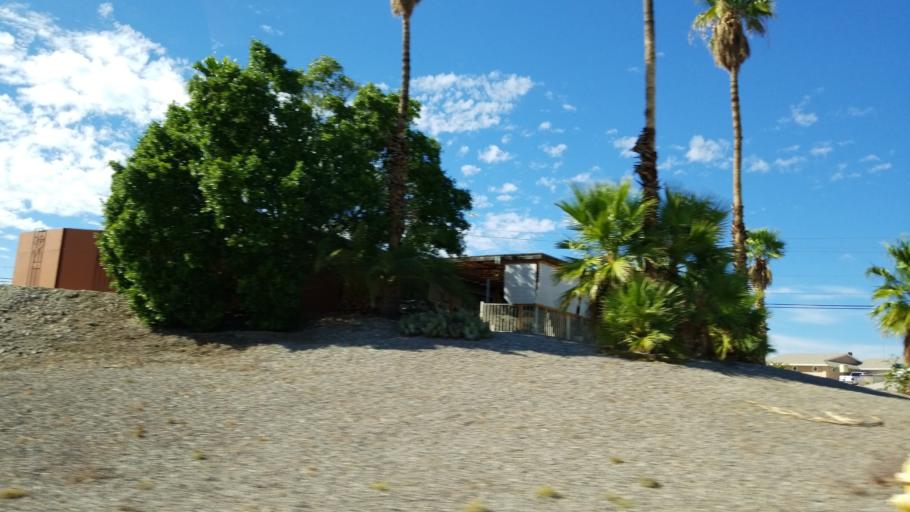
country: US
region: Arizona
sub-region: Mohave County
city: Lake Havasu City
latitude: 34.4872
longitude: -114.3016
